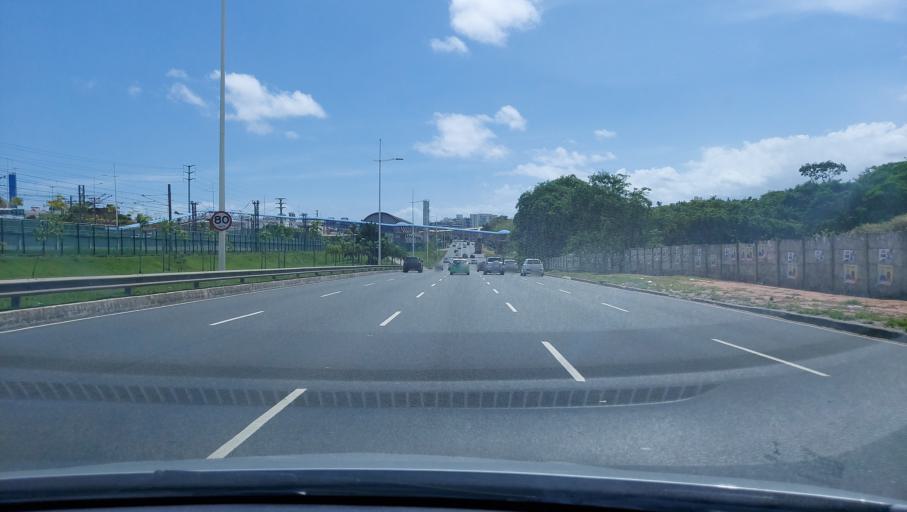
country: BR
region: Bahia
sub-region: Lauro De Freitas
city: Lauro de Freitas
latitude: -12.9317
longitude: -38.3917
